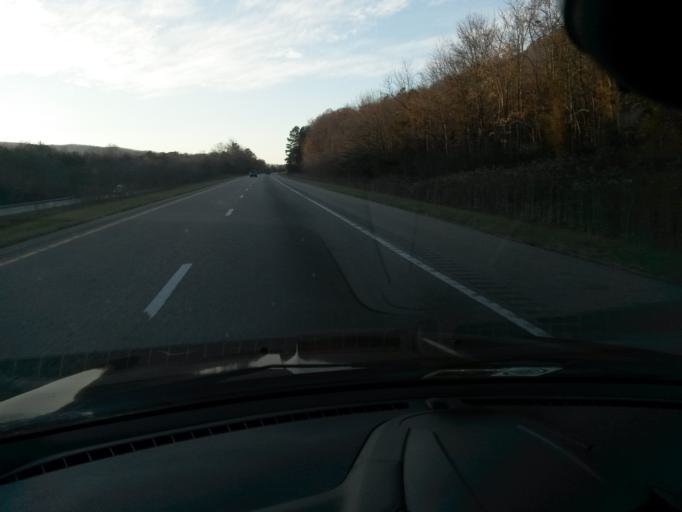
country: US
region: Virginia
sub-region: City of Lexington
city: Lexington
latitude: 37.8777
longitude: -79.5366
